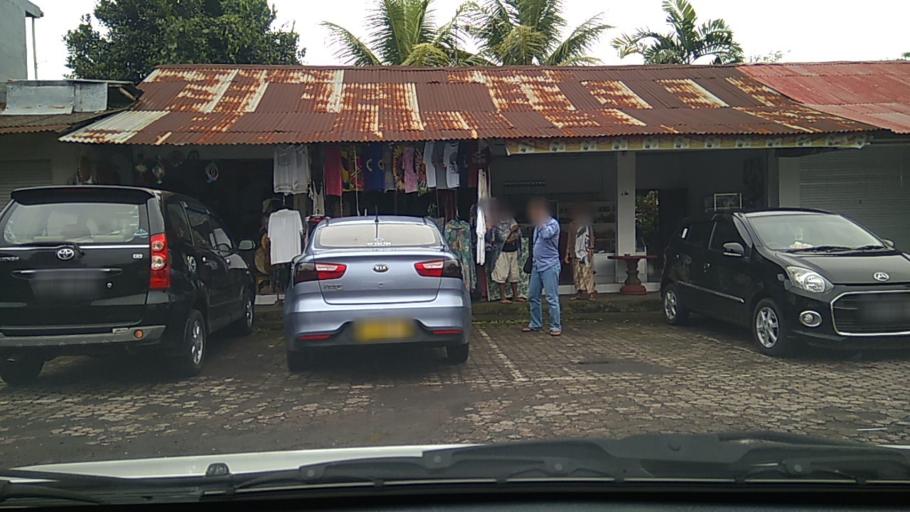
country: ID
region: Bali
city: Banjar Manukayaanyar
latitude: -8.4235
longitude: 115.3090
